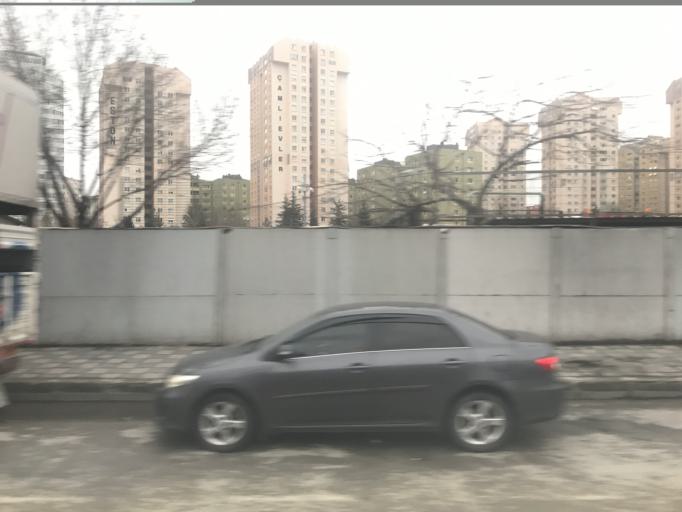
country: TR
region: Istanbul
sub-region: Atasehir
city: Atasehir
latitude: 40.9780
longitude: 29.1040
